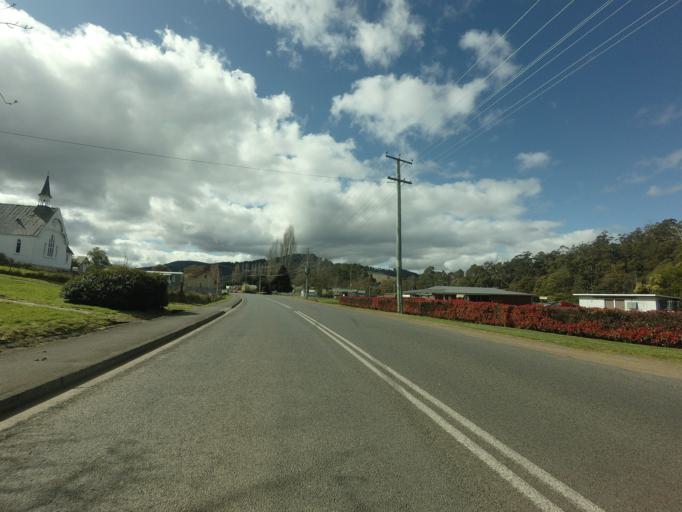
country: AU
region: Tasmania
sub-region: Huon Valley
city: Geeveston
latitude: -43.1698
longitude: 146.9259
